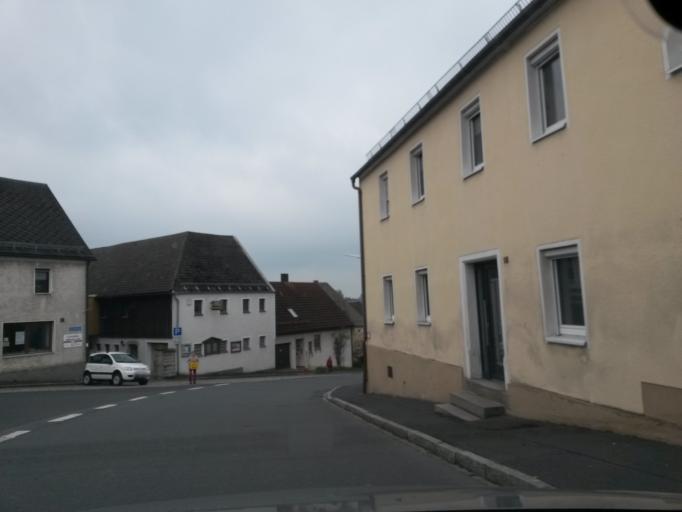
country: DE
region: Bavaria
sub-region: Upper Palatinate
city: Konradsreuth
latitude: 49.7836
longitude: 12.3096
